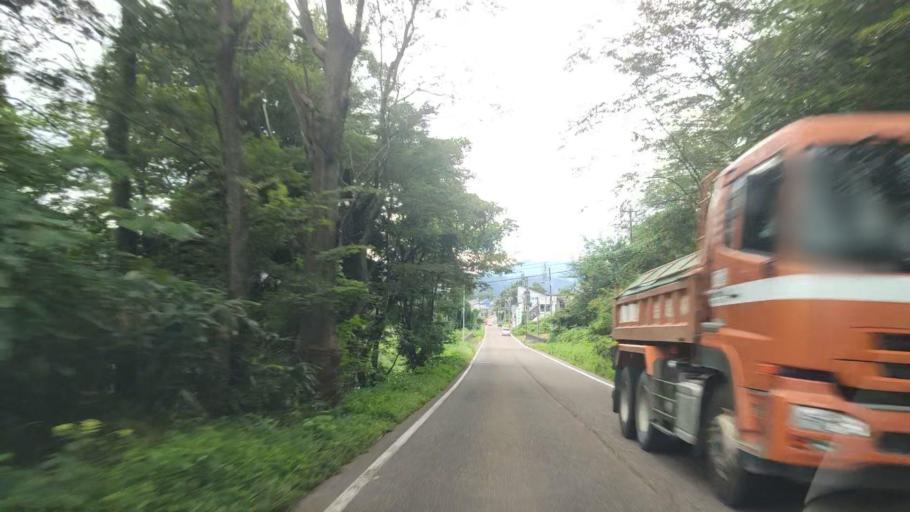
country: JP
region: Niigata
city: Arai
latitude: 36.9956
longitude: 138.2687
